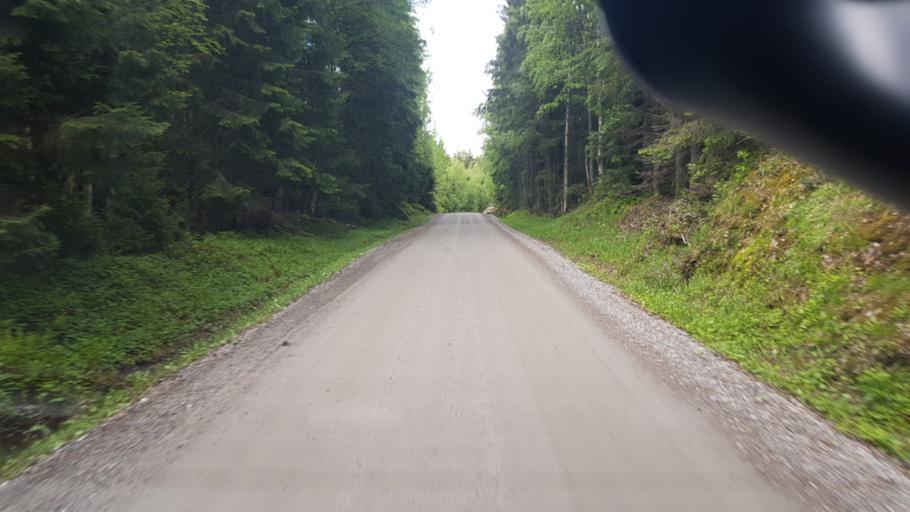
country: NO
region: Ostfold
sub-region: Romskog
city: Romskog
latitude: 59.7155
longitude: 11.9866
